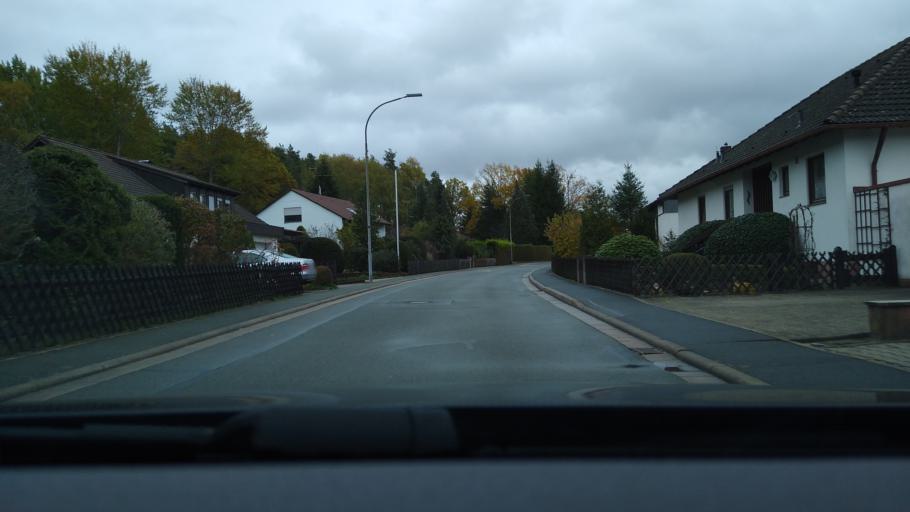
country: DE
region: Bavaria
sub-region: Regierungsbezirk Mittelfranken
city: Hemhofen
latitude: 49.6959
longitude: 10.9382
